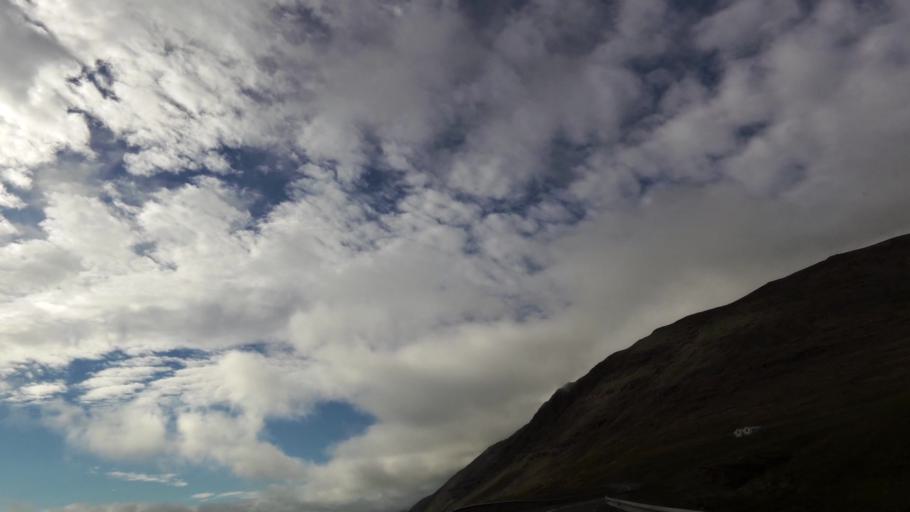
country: IS
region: West
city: Olafsvik
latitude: 65.5505
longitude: -23.8898
